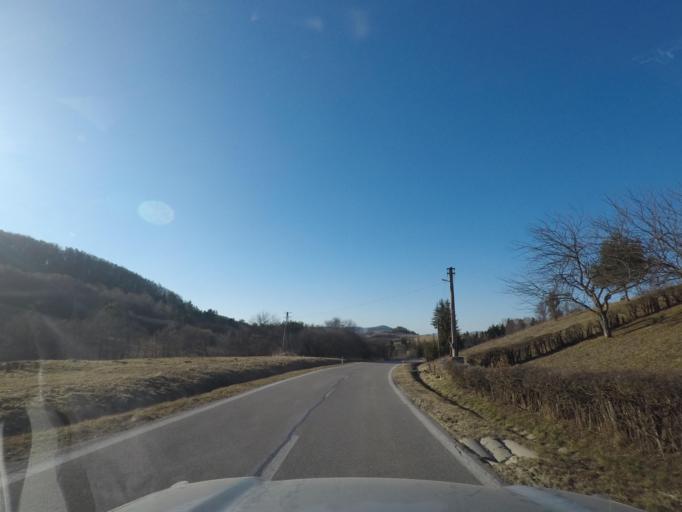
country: SK
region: Presovsky
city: Medzilaborce
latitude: 49.2440
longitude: 21.9351
